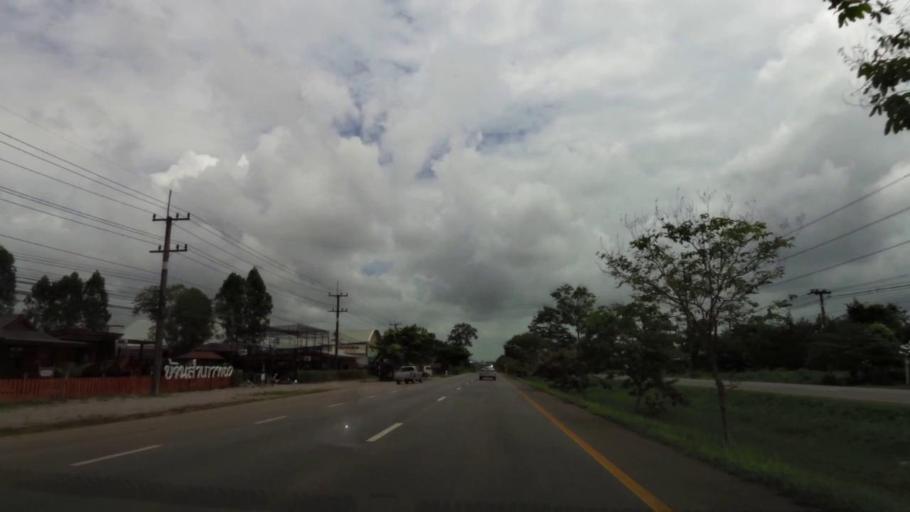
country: TH
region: Chanthaburi
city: Na Yai Am
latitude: 12.7567
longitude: 101.8606
